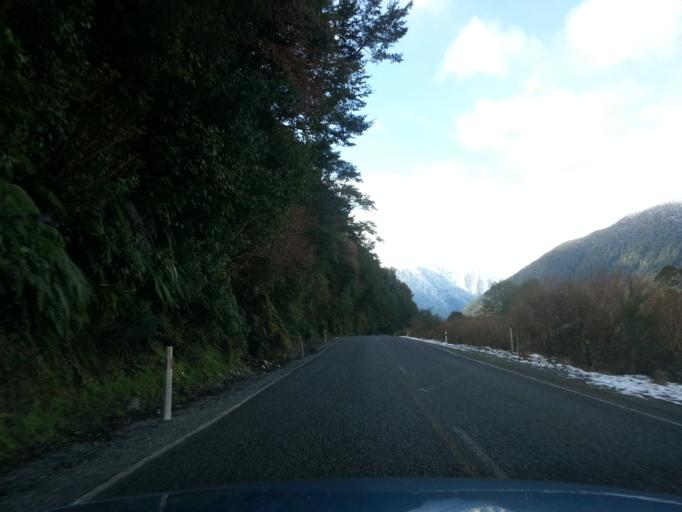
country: NZ
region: West Coast
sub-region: Grey District
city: Greymouth
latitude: -42.7837
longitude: 171.6071
